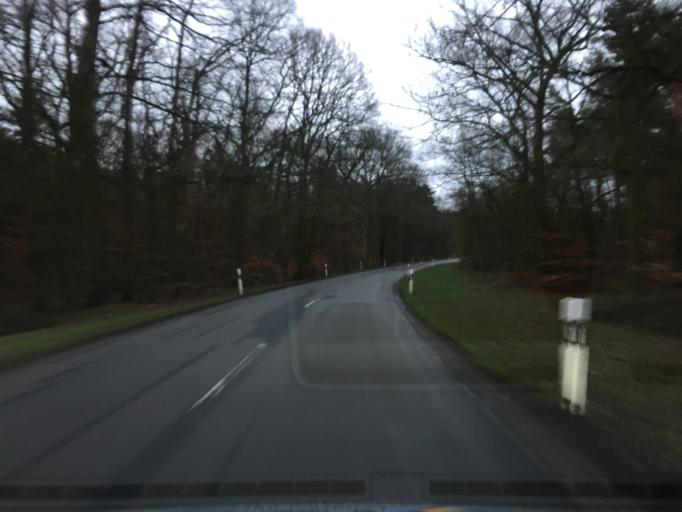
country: DE
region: Lower Saxony
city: Pennigsehl
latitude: 52.6501
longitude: 8.9965
